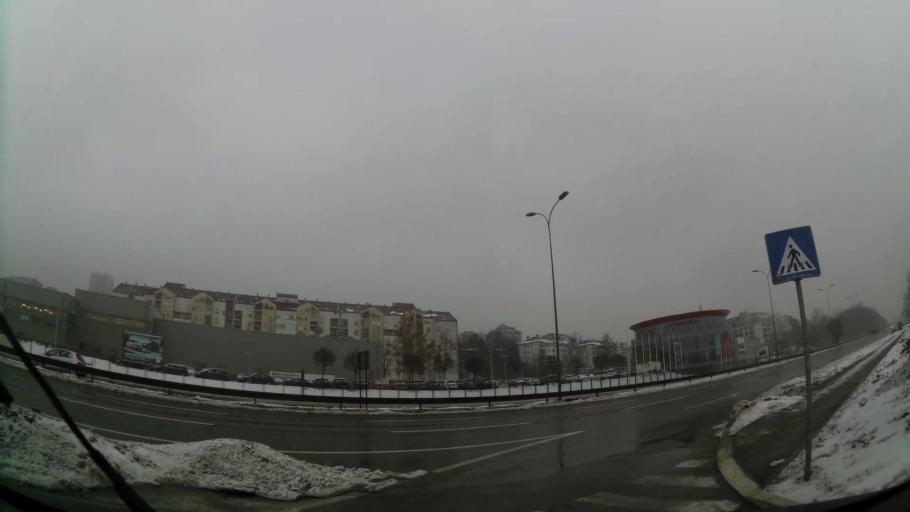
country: RS
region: Central Serbia
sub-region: Belgrade
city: Cukarica
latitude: 44.7840
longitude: 20.4106
